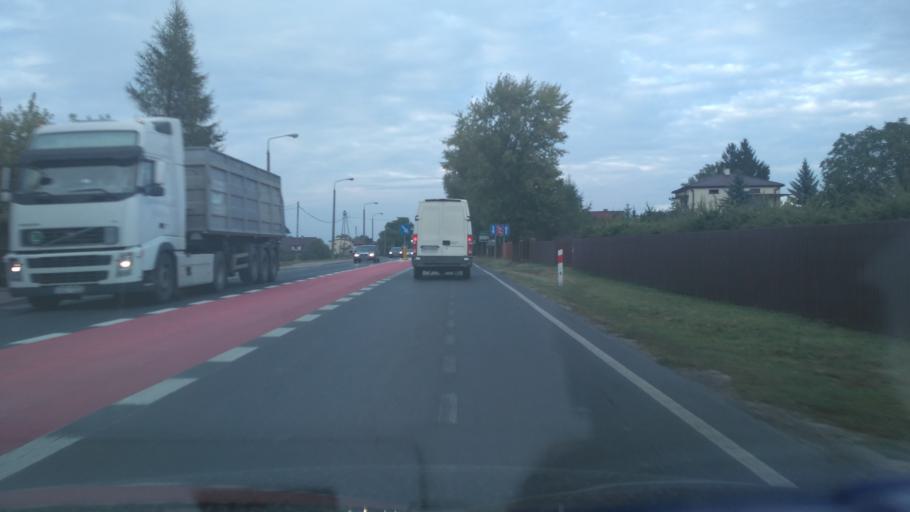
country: PL
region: Lublin Voivodeship
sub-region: Powiat lubelski
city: Jakubowice Murowane
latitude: 51.2689
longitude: 22.6380
